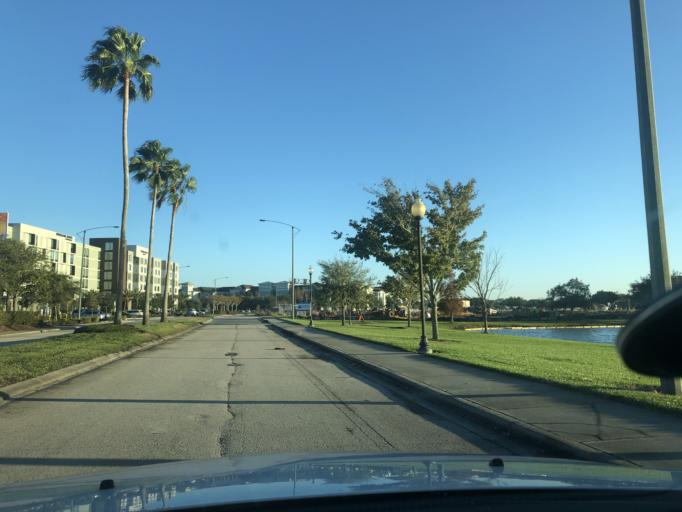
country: US
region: Florida
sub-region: Orange County
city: Oak Ridge
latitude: 28.4853
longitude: -81.4364
